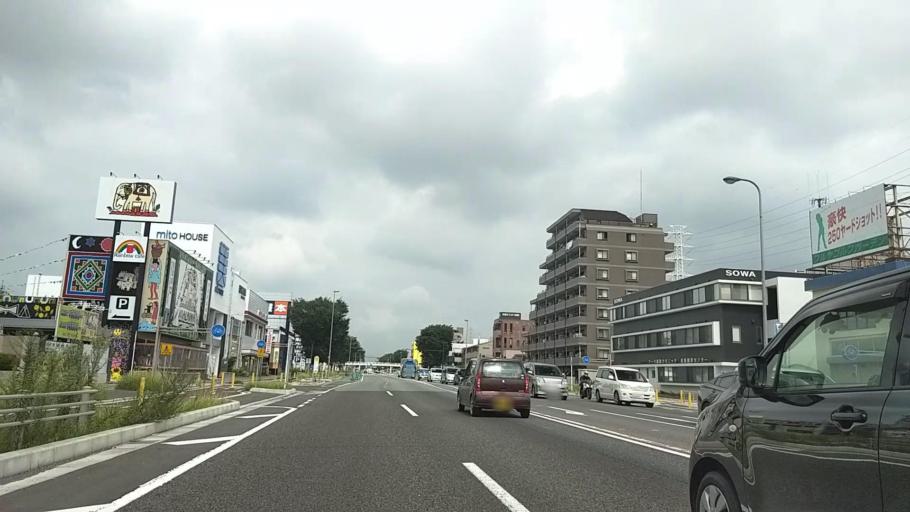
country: JP
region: Tokyo
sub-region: Machida-shi
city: Machida
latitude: 35.5671
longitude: 139.3864
